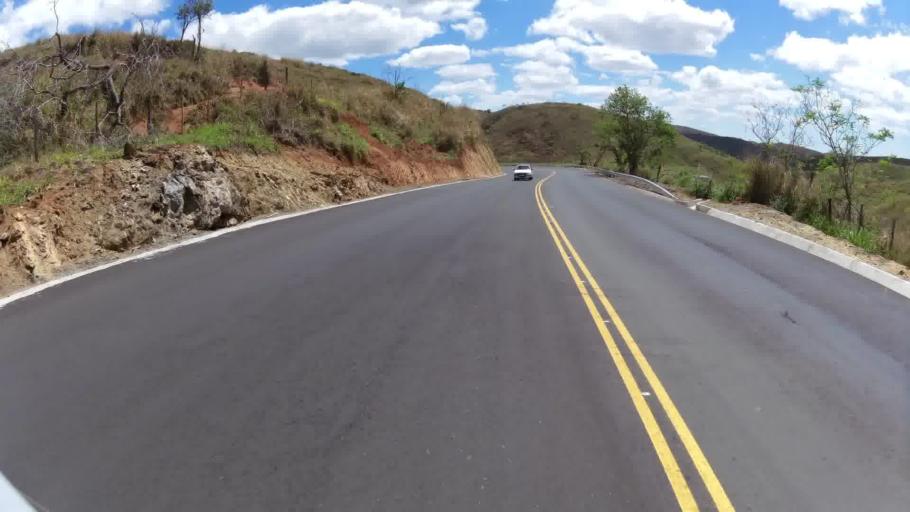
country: BR
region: Rio de Janeiro
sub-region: Itaperuna
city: Itaperuna
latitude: -21.2918
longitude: -41.8063
